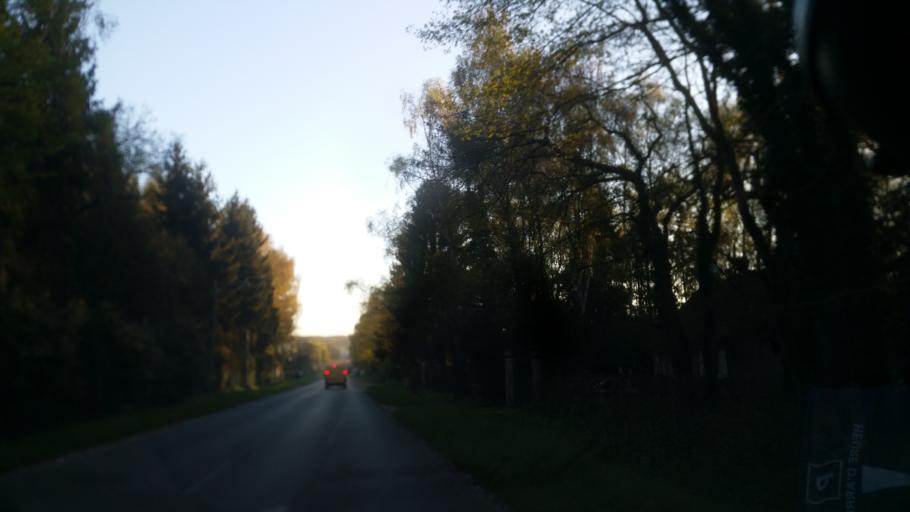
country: FR
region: Ile-de-France
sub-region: Departement de l'Essonne
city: Angervilliers
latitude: 48.5976
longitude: 2.0661
